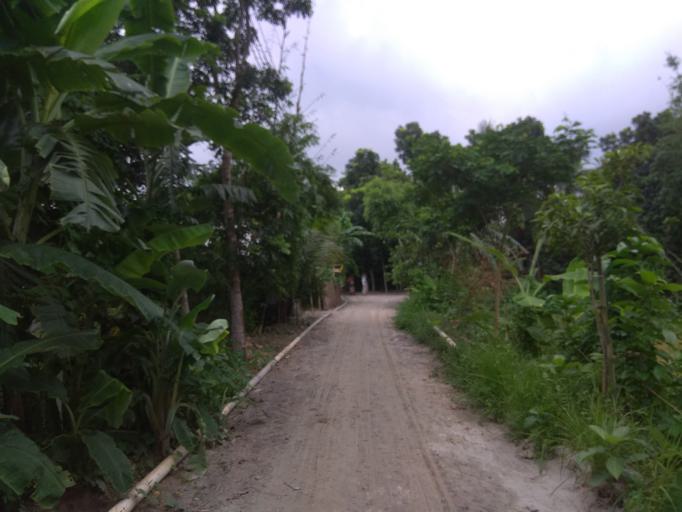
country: BD
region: Dhaka
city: Dohar
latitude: 23.4919
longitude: 90.0375
